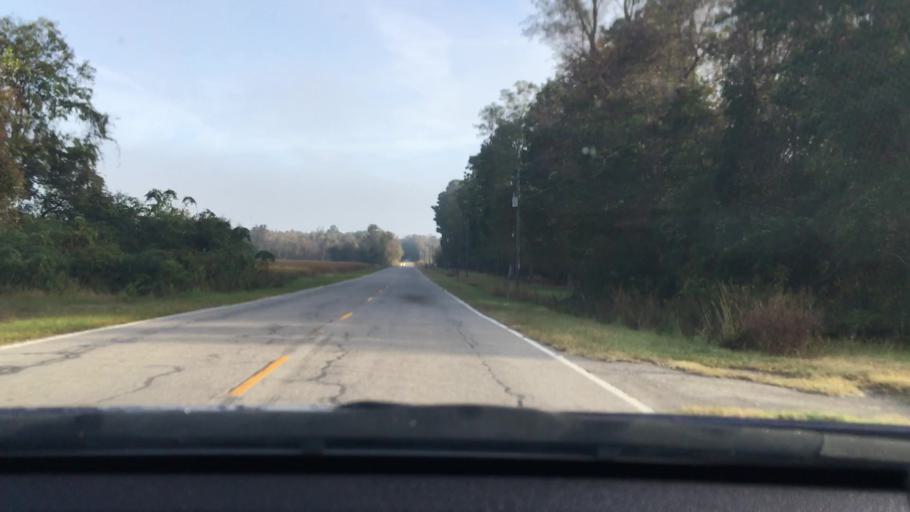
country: US
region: South Carolina
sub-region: Sumter County
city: East Sumter
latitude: 33.9906
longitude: -80.2938
